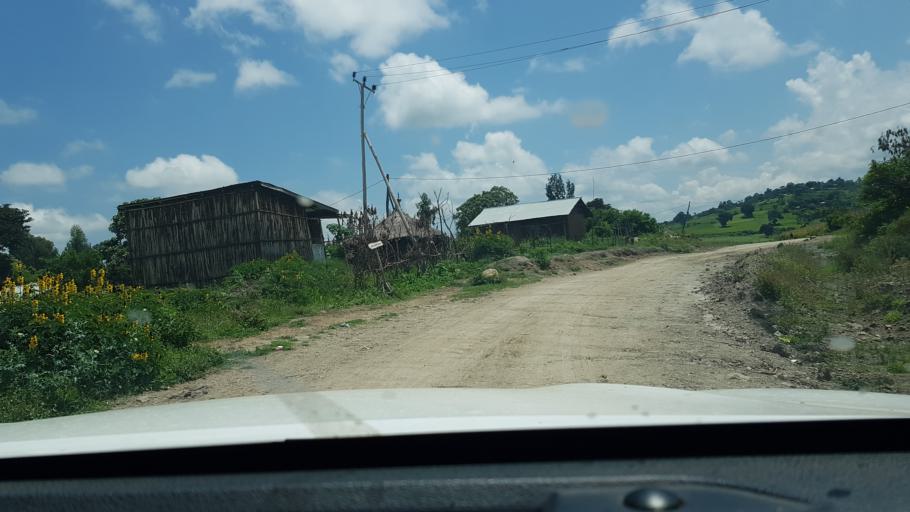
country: ET
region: Oromiya
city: Sirre
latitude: 8.4363
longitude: 39.8755
